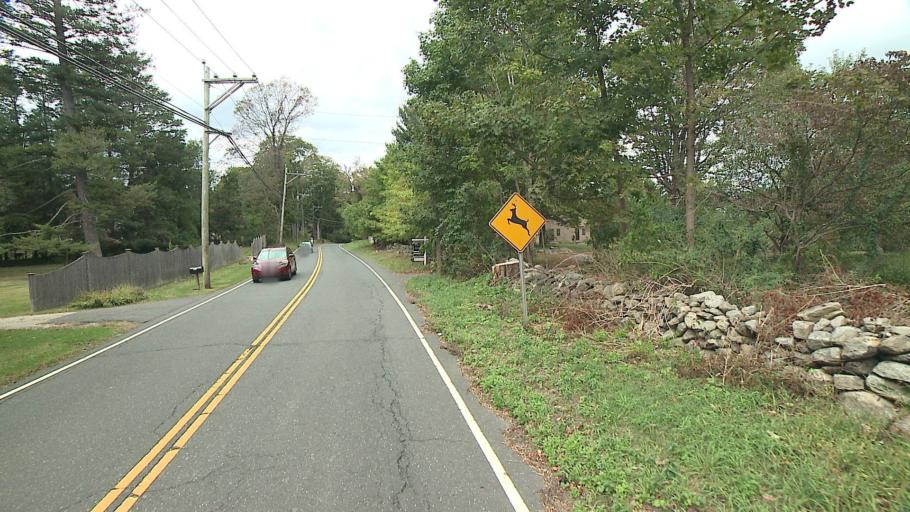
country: US
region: Connecticut
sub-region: Fairfield County
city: Ridgefield
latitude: 41.2530
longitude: -73.4913
